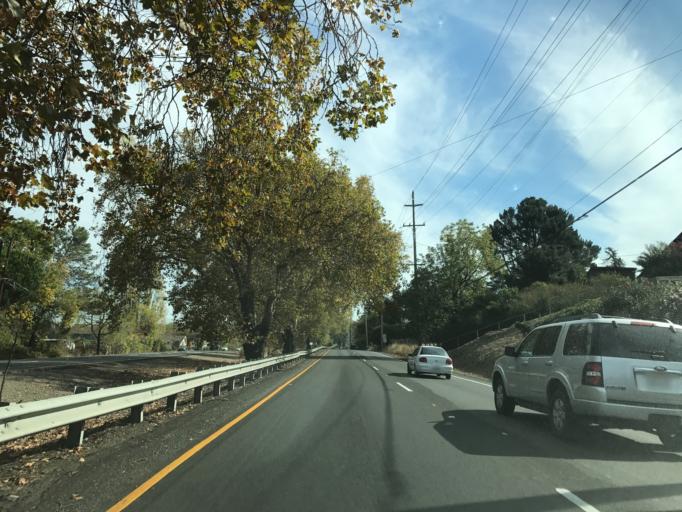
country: US
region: California
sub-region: Sonoma County
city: Petaluma
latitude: 38.2599
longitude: -122.6604
